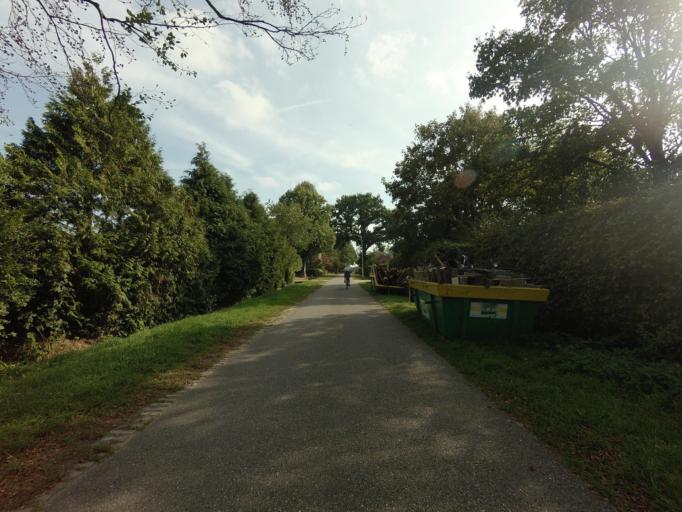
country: NL
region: Drenthe
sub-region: Gemeente Tynaarlo
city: Vries
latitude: 53.1196
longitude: 6.5699
